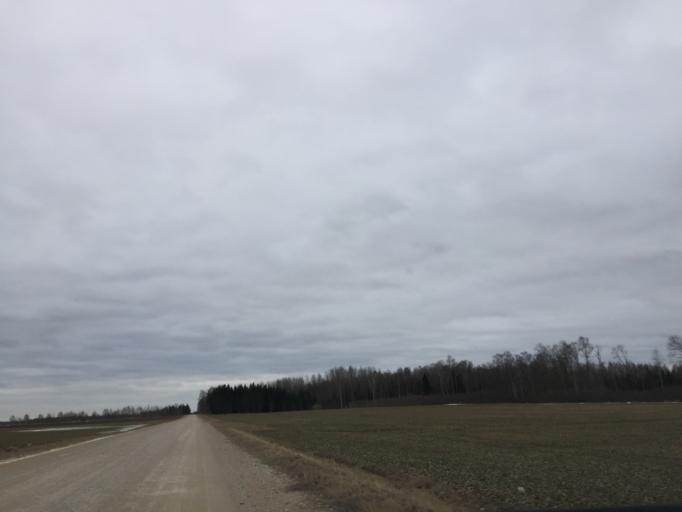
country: LT
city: Zagare
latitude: 56.3085
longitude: 23.2547
